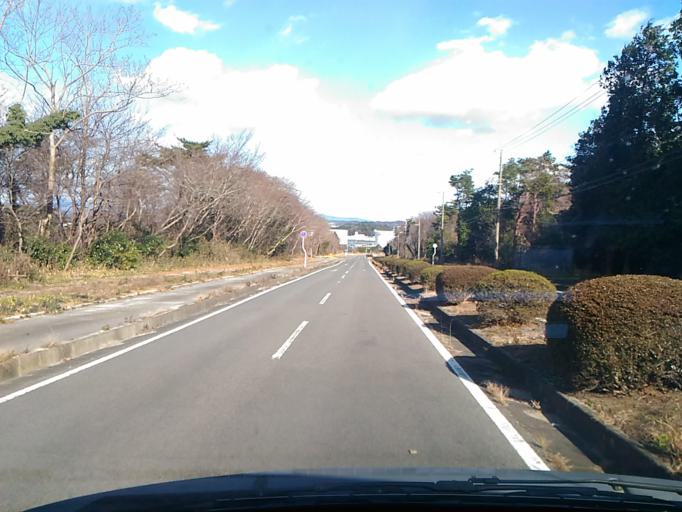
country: JP
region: Fukushima
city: Iwaki
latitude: 36.9237
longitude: 140.8523
